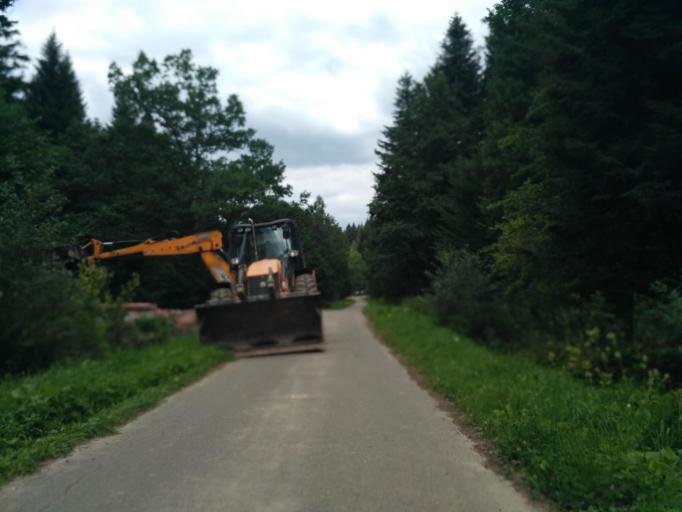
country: PL
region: Subcarpathian Voivodeship
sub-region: Powiat rzeszowski
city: Dynow
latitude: 49.7537
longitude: 22.2918
